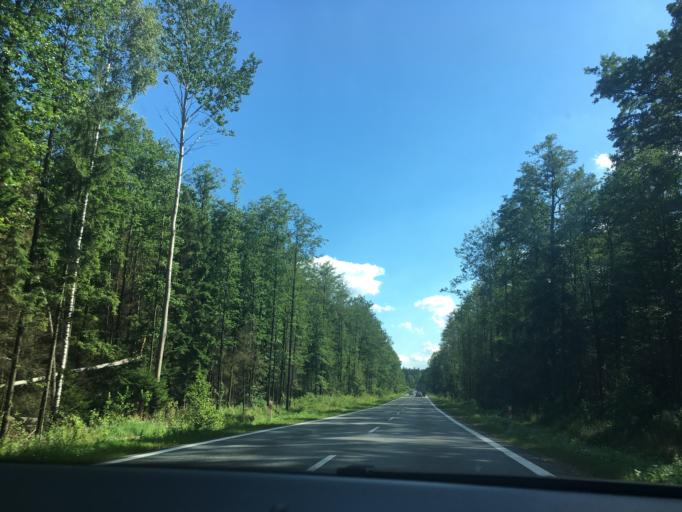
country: PL
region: Podlasie
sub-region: Powiat bialostocki
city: Wasilkow
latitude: 53.2801
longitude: 23.1211
